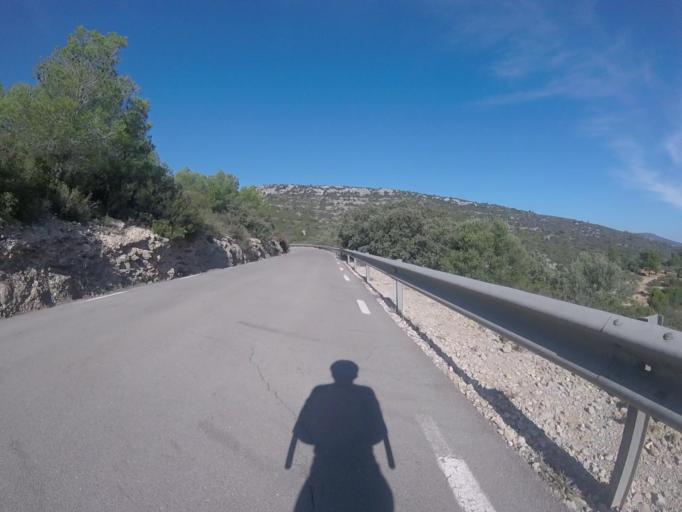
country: ES
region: Valencia
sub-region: Provincia de Castello
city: Sarratella
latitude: 40.2723
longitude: 0.0521
